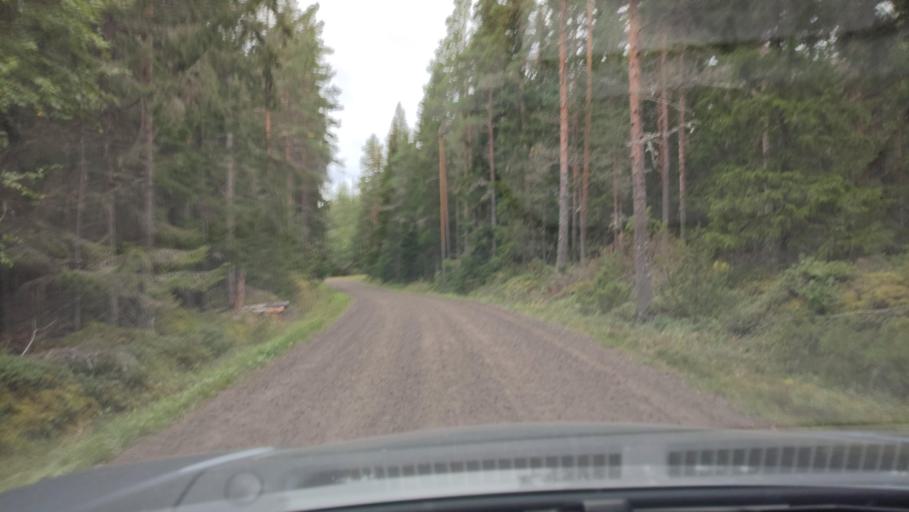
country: FI
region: Southern Ostrobothnia
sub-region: Suupohja
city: Karijoki
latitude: 62.2306
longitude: 21.5736
